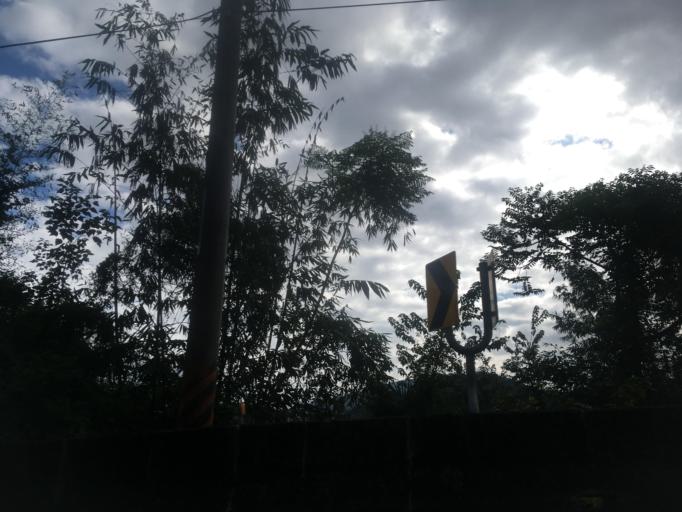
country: TW
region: Taiwan
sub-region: Yilan
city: Yilan
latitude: 24.6597
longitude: 121.5875
